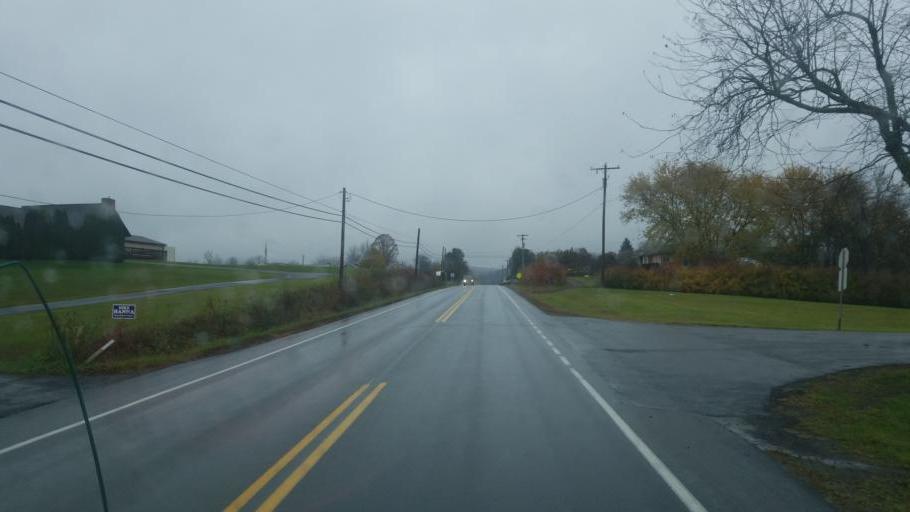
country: US
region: Pennsylvania
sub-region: Clinton County
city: Mill Hall
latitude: 41.0682
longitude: -77.6004
